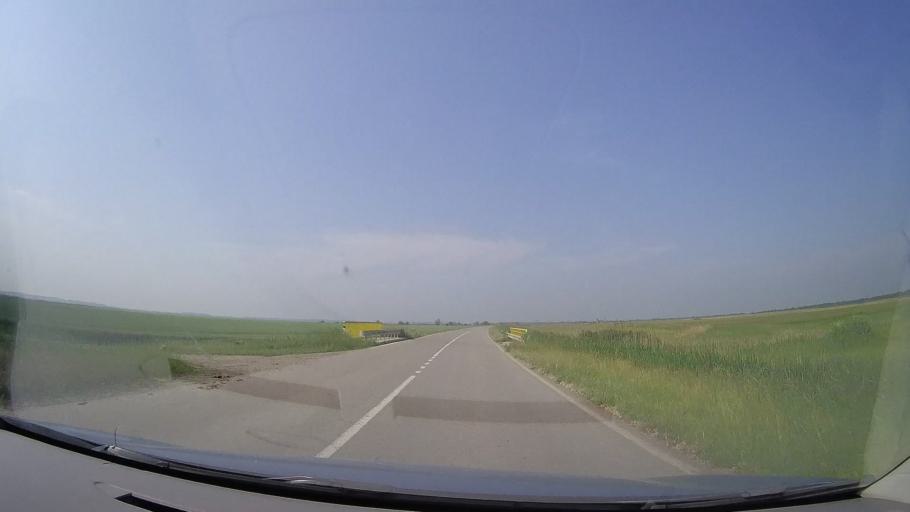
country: RS
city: Jasa Tomic
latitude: 45.4121
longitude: 20.8287
